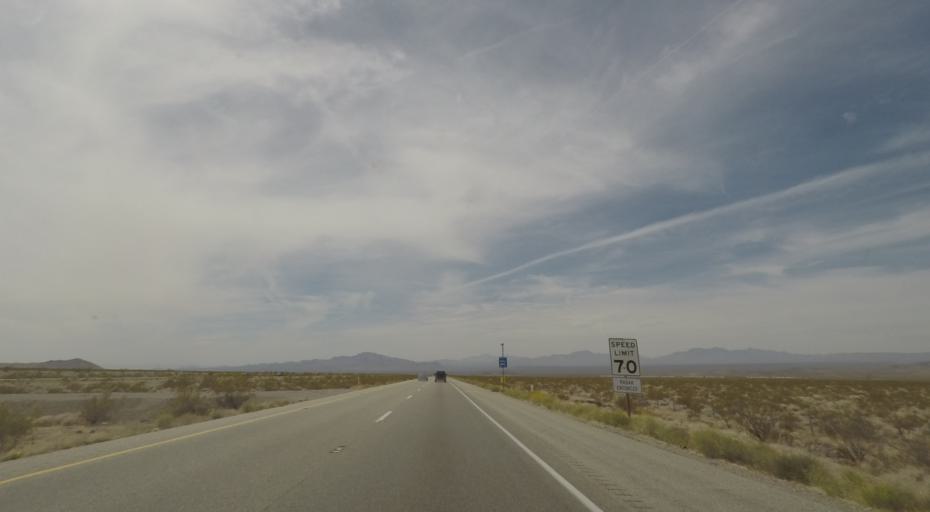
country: US
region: California
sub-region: San Bernardino County
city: Needles
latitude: 34.8230
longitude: -115.1060
